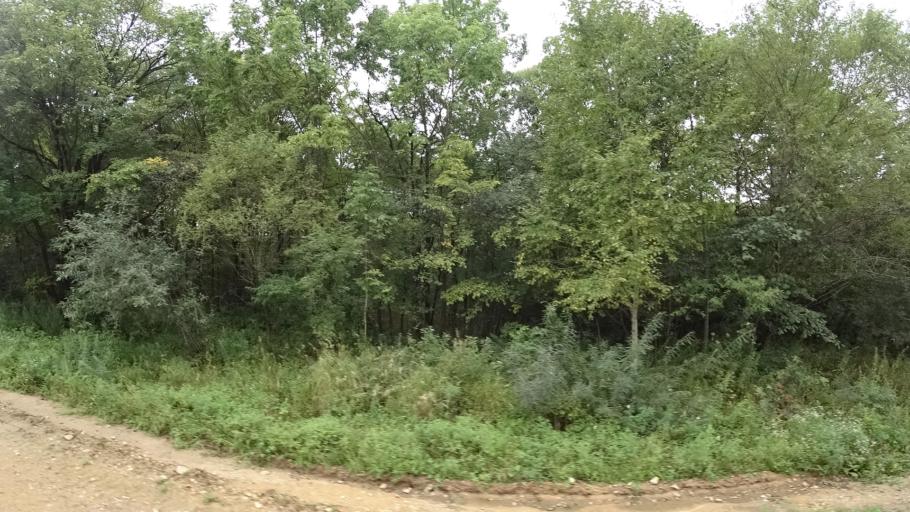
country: RU
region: Primorskiy
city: Rettikhovka
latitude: 44.0618
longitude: 132.6539
